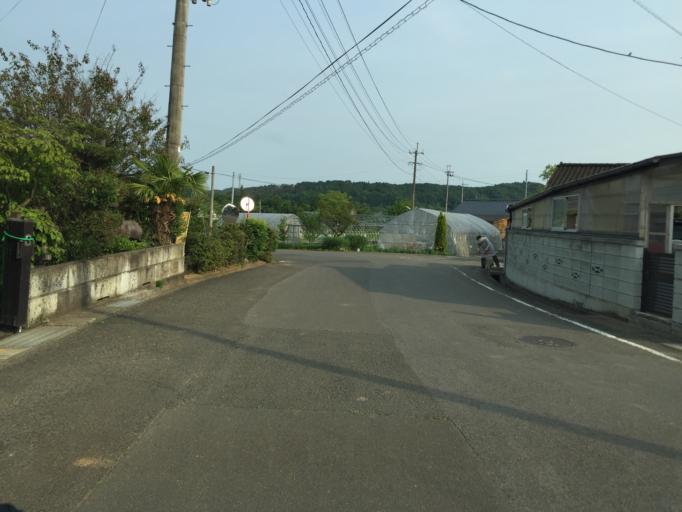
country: JP
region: Fukushima
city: Fukushima-shi
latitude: 37.7169
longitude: 140.4342
